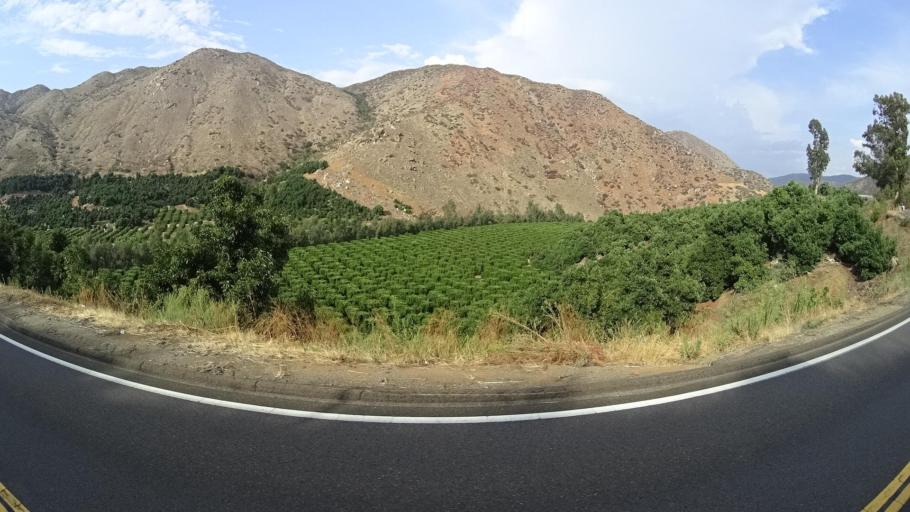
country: US
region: California
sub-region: San Diego County
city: San Pasqual
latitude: 33.0858
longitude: -116.9257
